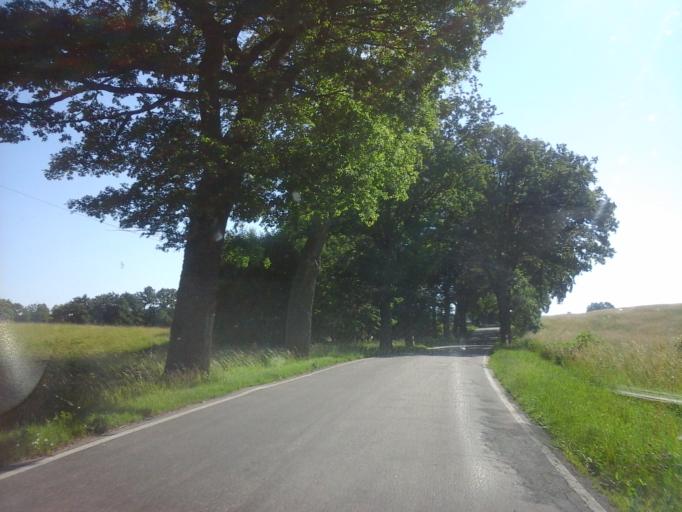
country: PL
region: West Pomeranian Voivodeship
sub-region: Powiat drawski
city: Drawsko Pomorskie
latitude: 53.5743
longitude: 15.8611
